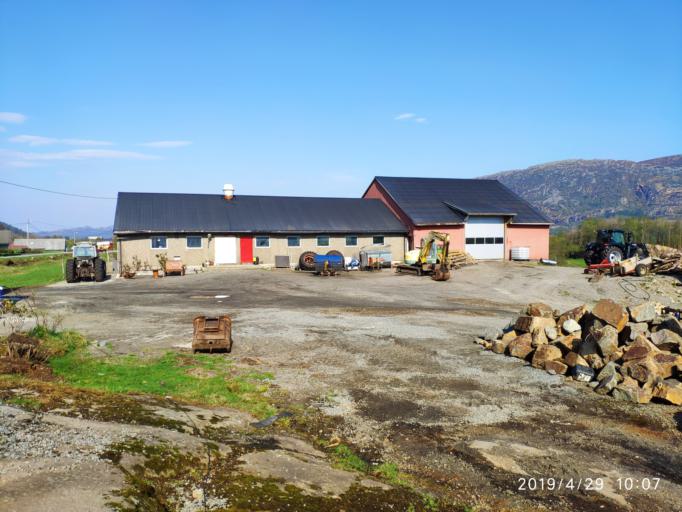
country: NO
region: Rogaland
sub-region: Sokndal
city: Hauge i Dalane
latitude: 58.5399
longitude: 6.3041
